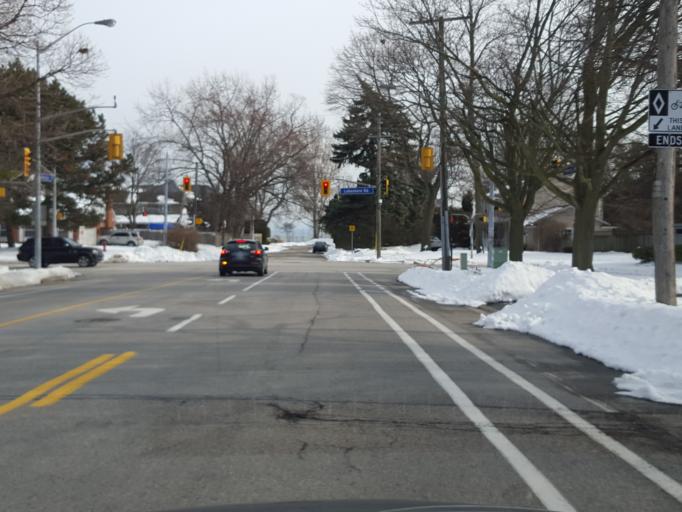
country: CA
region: Ontario
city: Burlington
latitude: 43.3471
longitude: -79.7618
